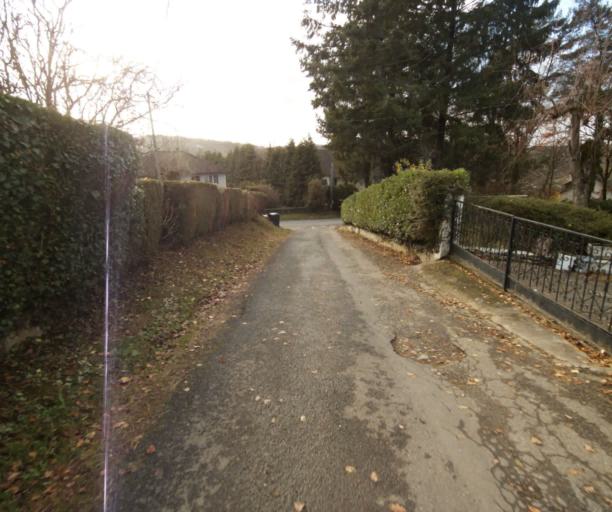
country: FR
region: Limousin
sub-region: Departement de la Correze
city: Laguenne
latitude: 45.2346
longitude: 1.7868
